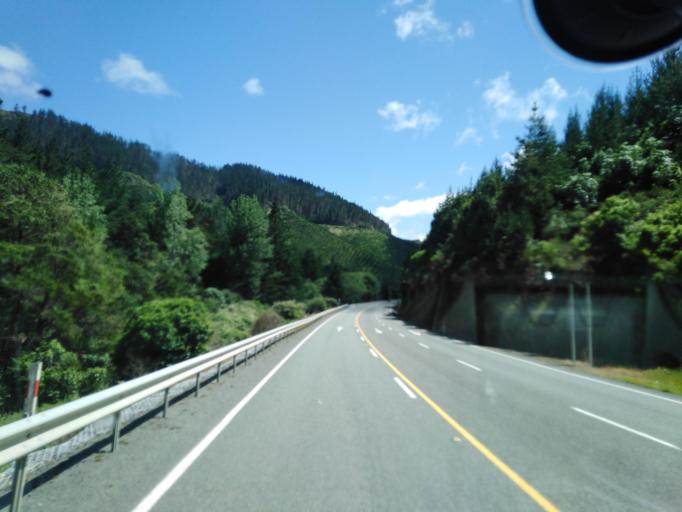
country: NZ
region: Nelson
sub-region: Nelson City
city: Nelson
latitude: -41.1825
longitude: 173.5596
